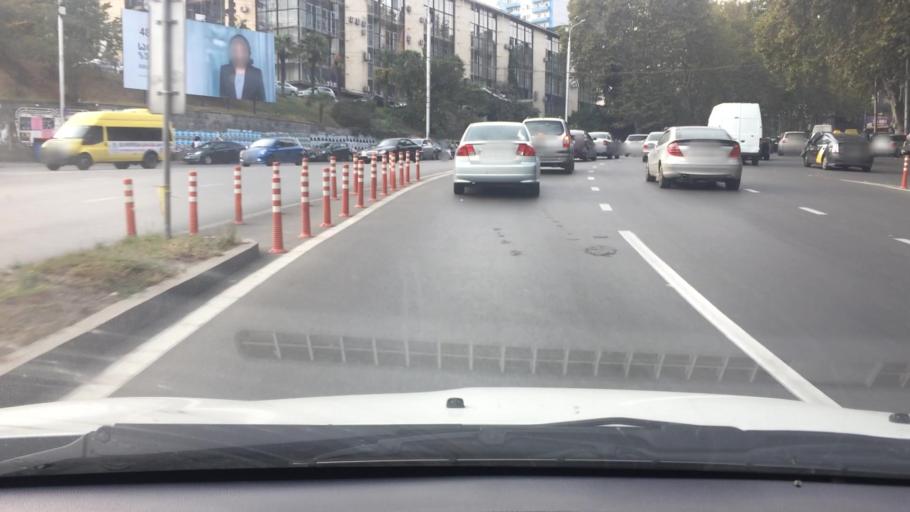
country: GE
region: T'bilisi
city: Tbilisi
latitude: 41.7140
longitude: 44.7805
